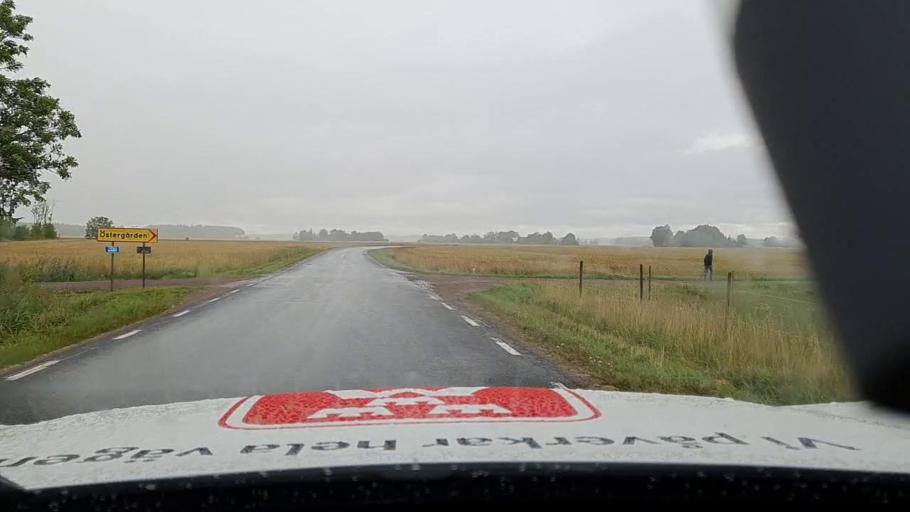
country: SE
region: Vaestra Goetaland
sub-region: Toreboda Kommun
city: Toereboda
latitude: 58.6528
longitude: 14.1065
